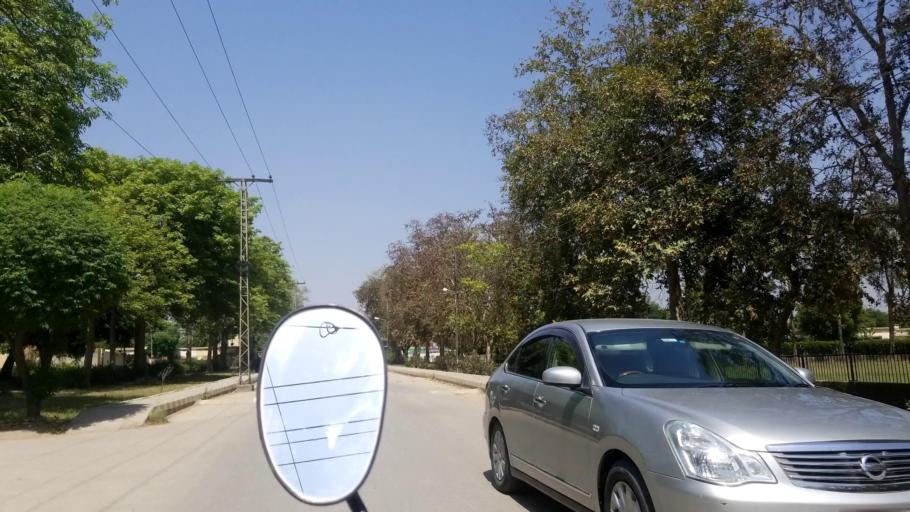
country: PK
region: Khyber Pakhtunkhwa
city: Peshawar
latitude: 34.0169
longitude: 71.4836
